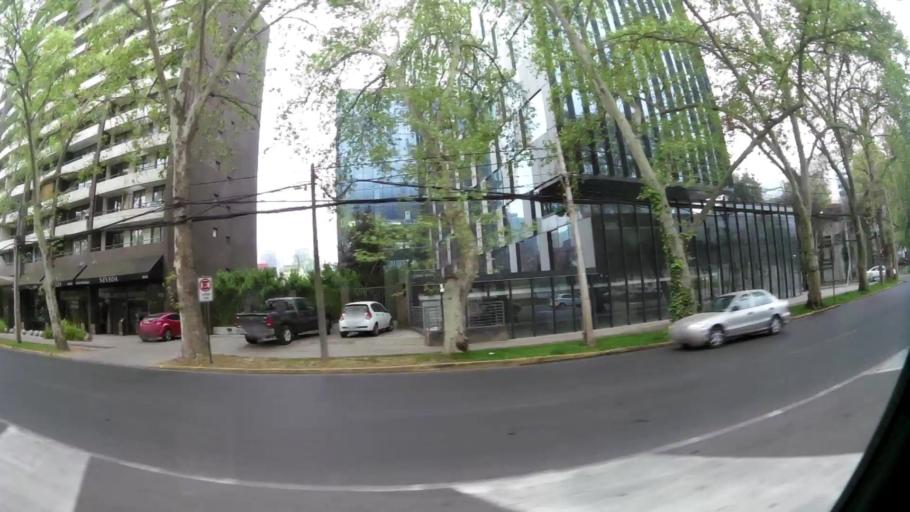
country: CL
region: Santiago Metropolitan
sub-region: Provincia de Santiago
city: Santiago
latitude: -33.4248
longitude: -70.6214
